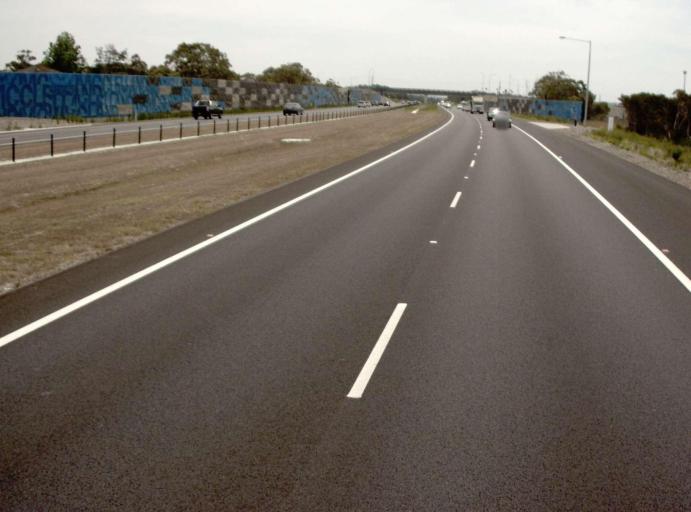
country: AU
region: Victoria
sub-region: Frankston
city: Langwarrin
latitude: -38.1461
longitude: 145.1729
